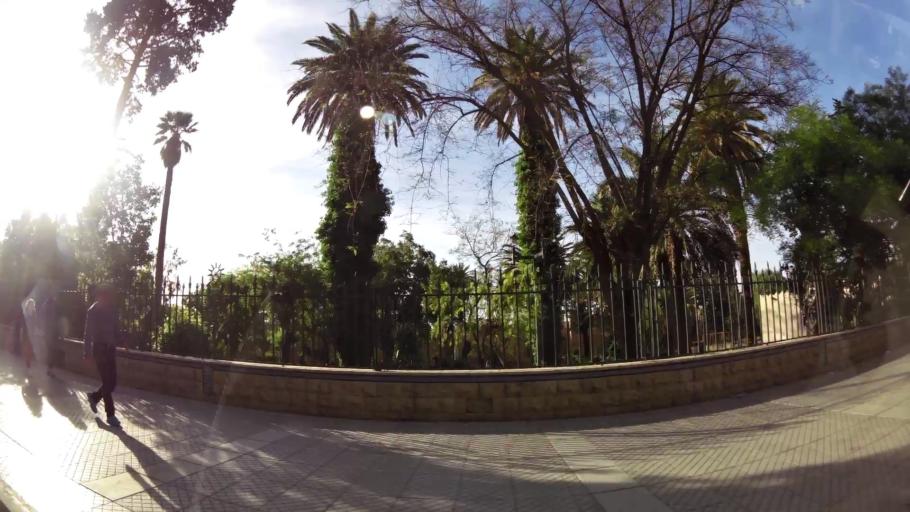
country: MA
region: Oriental
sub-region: Oujda-Angad
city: Oujda
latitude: 34.6770
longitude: -1.9128
